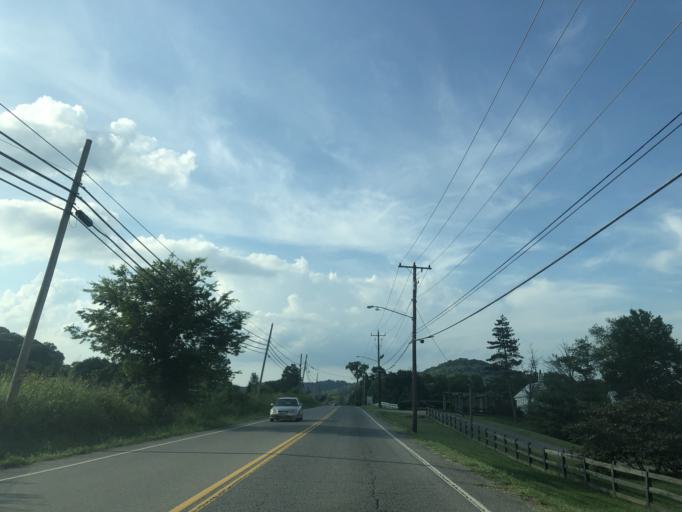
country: US
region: Tennessee
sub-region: Davidson County
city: Nashville
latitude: 36.2576
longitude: -86.8302
